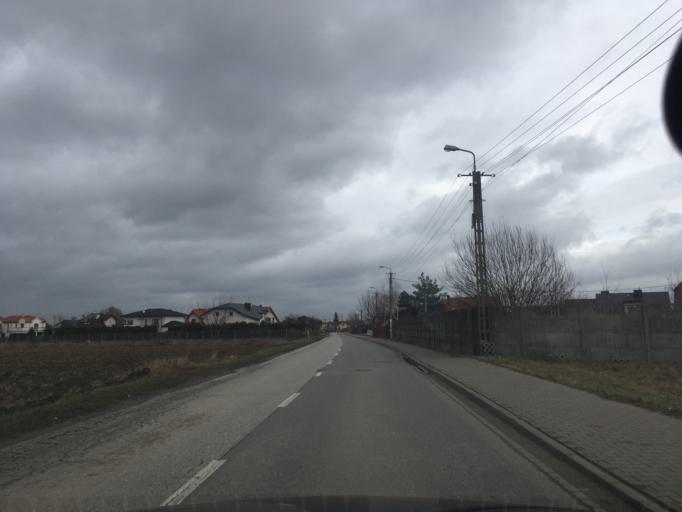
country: PL
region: Masovian Voivodeship
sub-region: Powiat pruszkowski
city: Rybie
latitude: 52.1236
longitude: 20.9515
